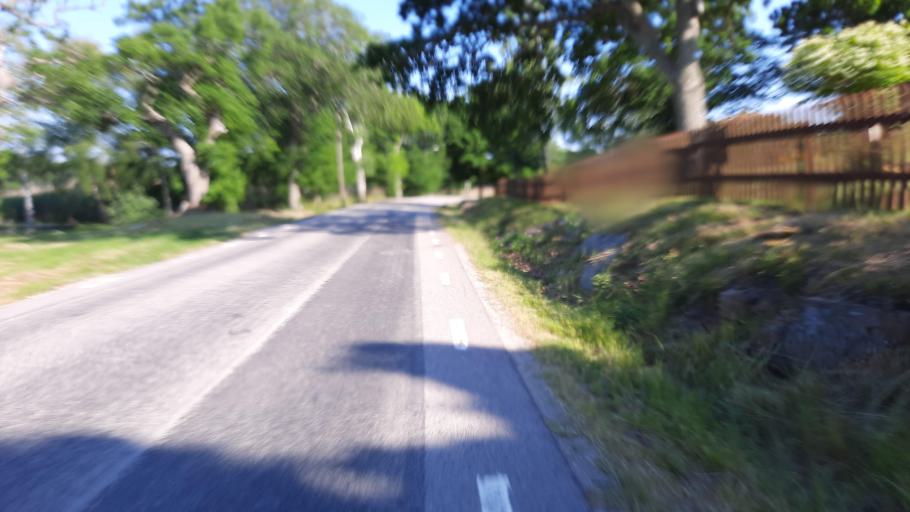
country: SE
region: Blekinge
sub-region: Karlskrona Kommun
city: Sturko
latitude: 56.0984
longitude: 15.6942
